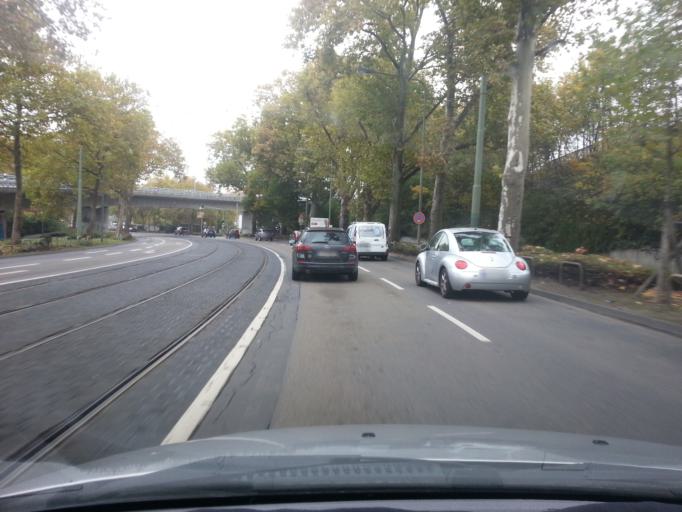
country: DE
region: Hesse
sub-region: Regierungsbezirk Darmstadt
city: Offenbach
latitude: 50.1221
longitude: 8.7282
